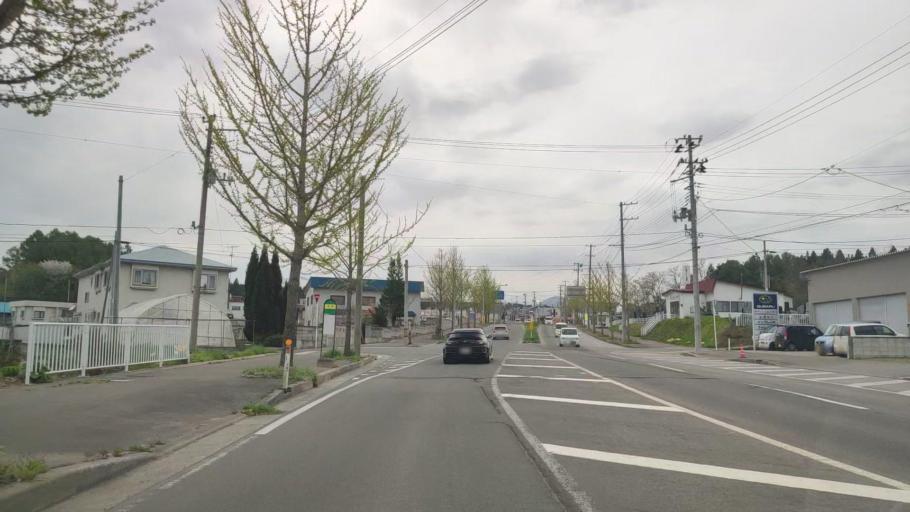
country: JP
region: Aomori
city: Aomori Shi
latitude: 40.7918
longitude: 140.7866
